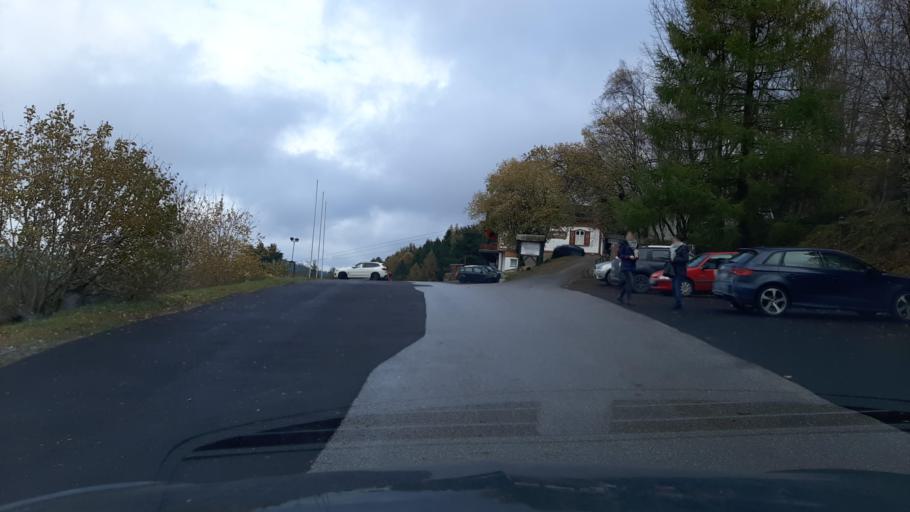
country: DE
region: Hesse
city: Willingen
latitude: 51.2857
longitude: 8.6039
